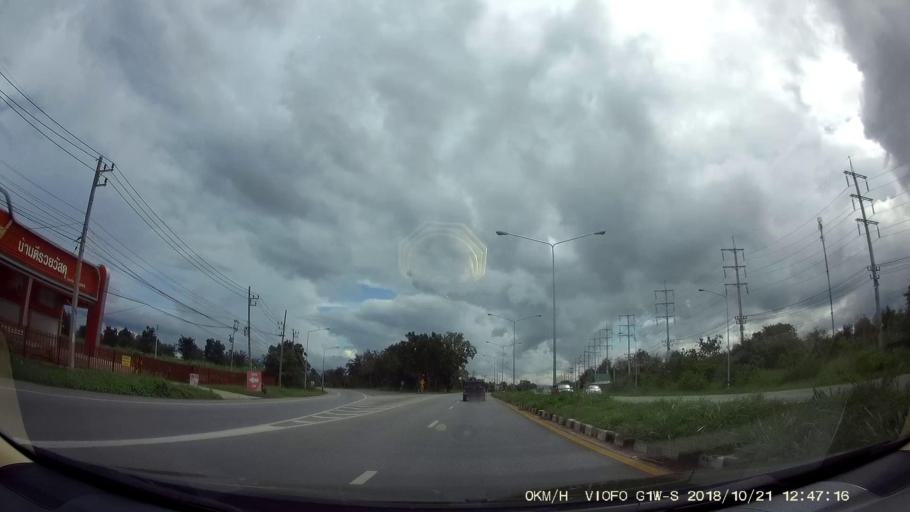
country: TH
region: Nakhon Ratchasima
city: Amphoe Sikhiu
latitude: 14.9307
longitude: 101.6836
